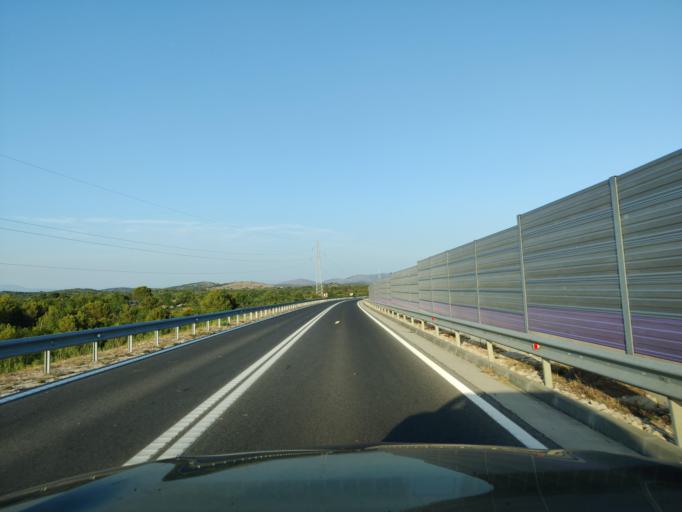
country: HR
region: Sibensko-Kniniska
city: Vodice
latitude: 43.7751
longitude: 15.7807
